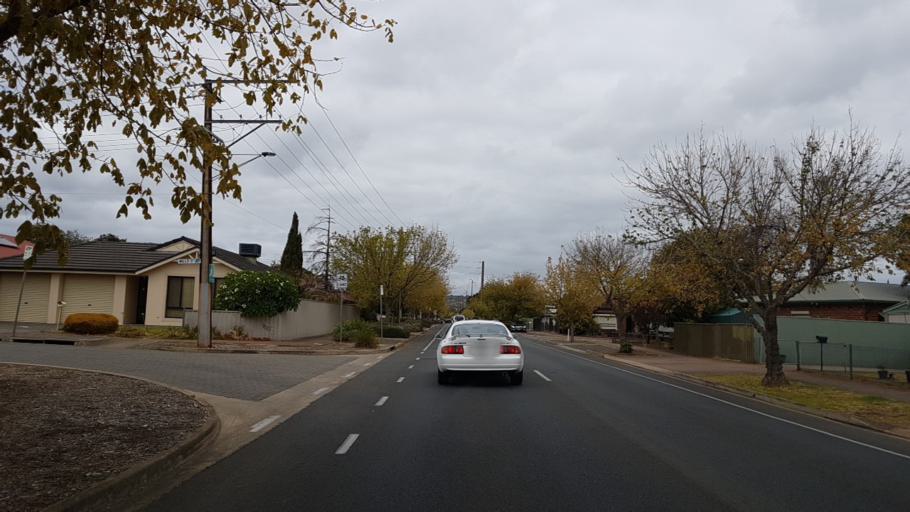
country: AU
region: South Australia
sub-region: Marion
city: Clovelly Park
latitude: -35.0060
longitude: 138.5657
